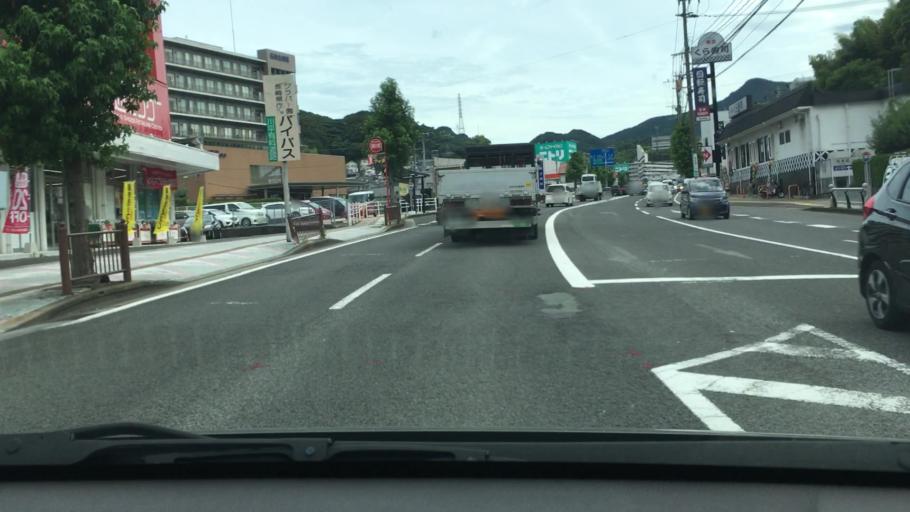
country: JP
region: Nagasaki
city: Togitsu
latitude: 32.8219
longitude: 129.8485
